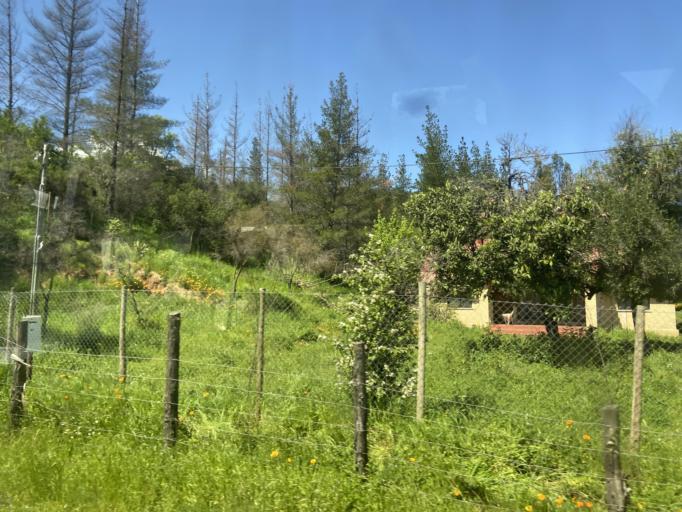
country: CL
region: Valparaiso
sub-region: Provincia de Marga Marga
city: Villa Alemana
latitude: -33.1879
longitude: -71.2965
